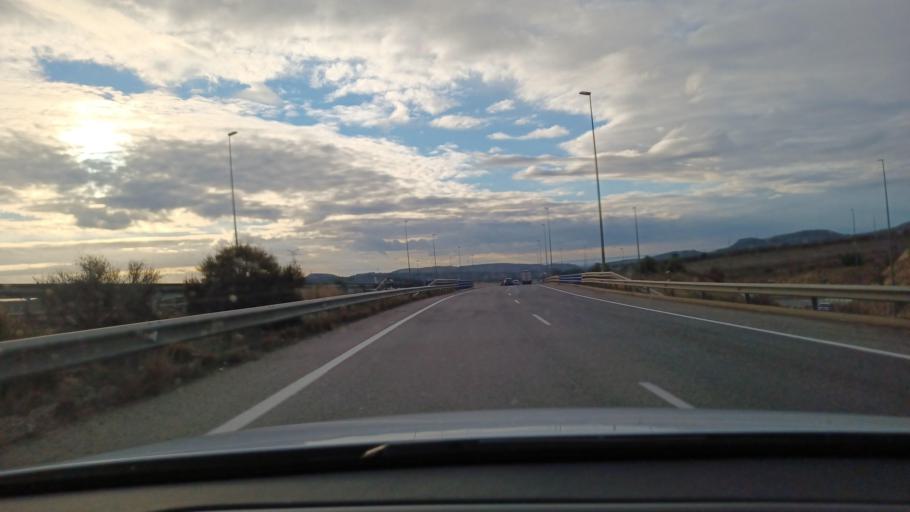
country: ES
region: Valencia
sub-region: Provincia de Alicante
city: Monforte del Cid
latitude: 38.3498
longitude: -0.6701
